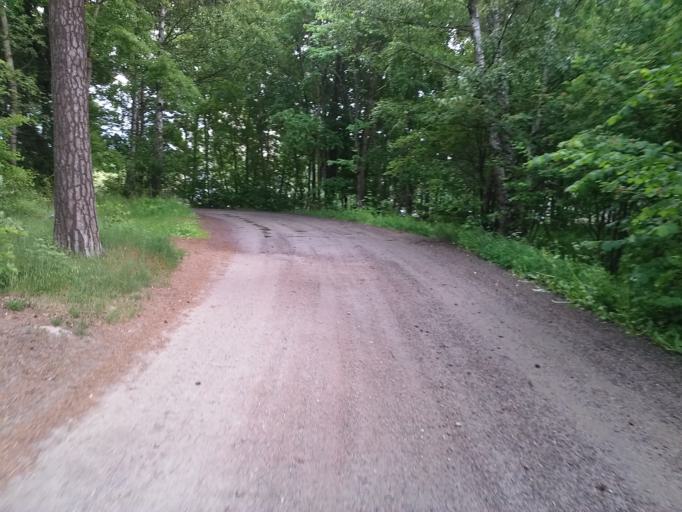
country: FI
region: Varsinais-Suomi
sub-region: Turku
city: Turku
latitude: 60.4753
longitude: 22.2250
